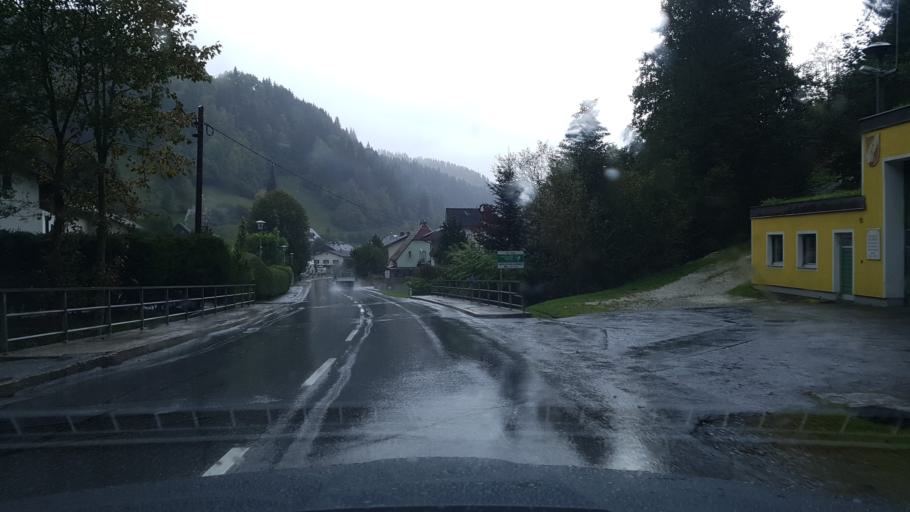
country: AT
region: Styria
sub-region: Politischer Bezirk Voitsberg
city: Salla
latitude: 47.1065
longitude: 14.9702
